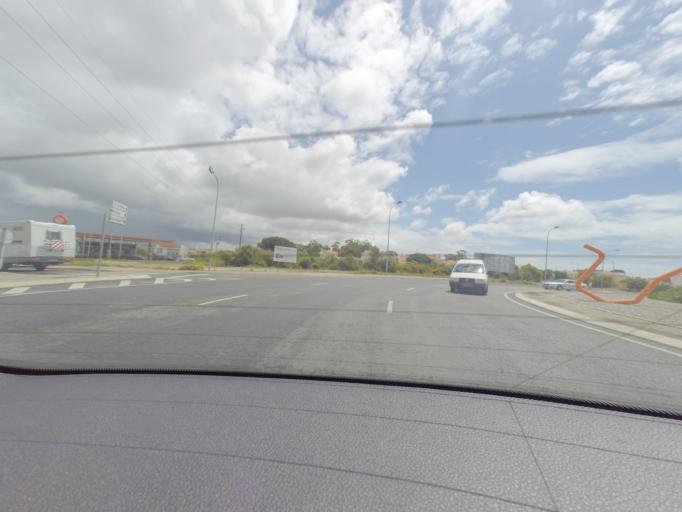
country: PT
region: Lisbon
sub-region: Cascais
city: Alcabideche
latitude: 38.7352
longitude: -9.3886
